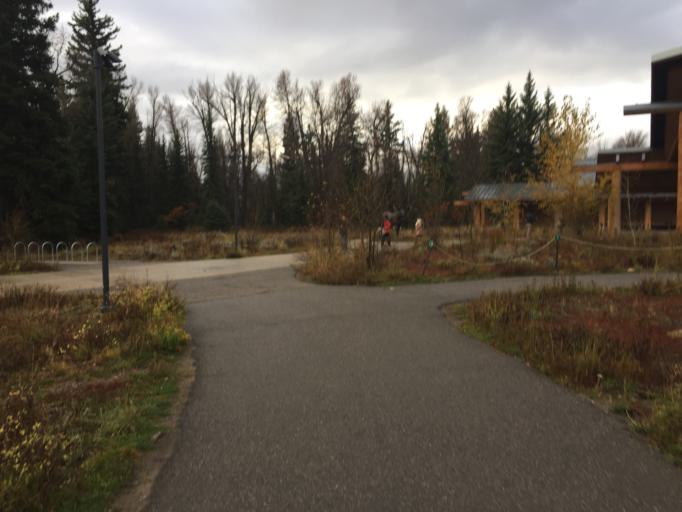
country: US
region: Wyoming
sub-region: Teton County
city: Jackson
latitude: 43.6534
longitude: -110.7179
